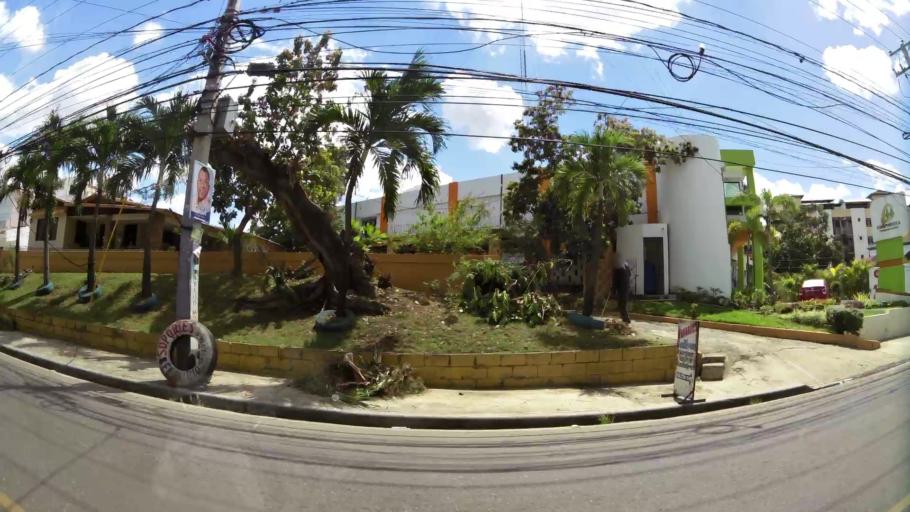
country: DO
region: Santiago
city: Santiago de los Caballeros
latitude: 19.4743
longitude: -70.6786
